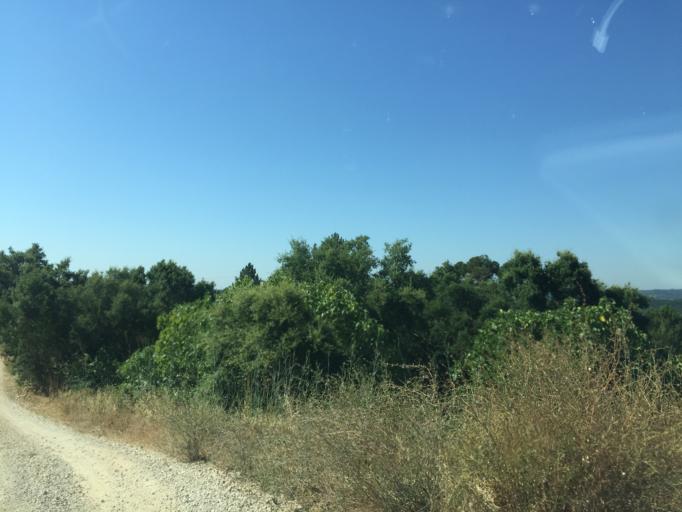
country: PT
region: Santarem
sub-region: Constancia
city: Constancia
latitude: 39.5526
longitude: -8.3262
